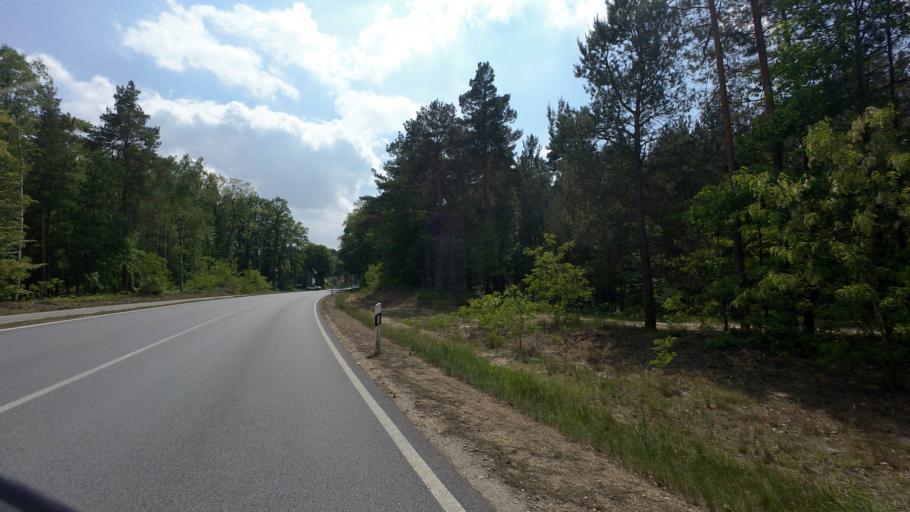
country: DE
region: Saxony
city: Rietschen
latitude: 51.4147
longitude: 14.7885
